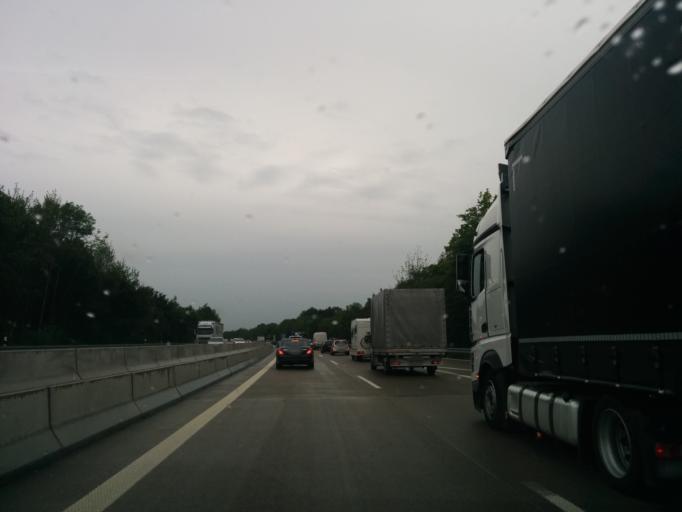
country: DE
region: Bavaria
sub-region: Regierungsbezirk Unterfranken
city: Martinsheim
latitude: 49.6267
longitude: 10.1763
